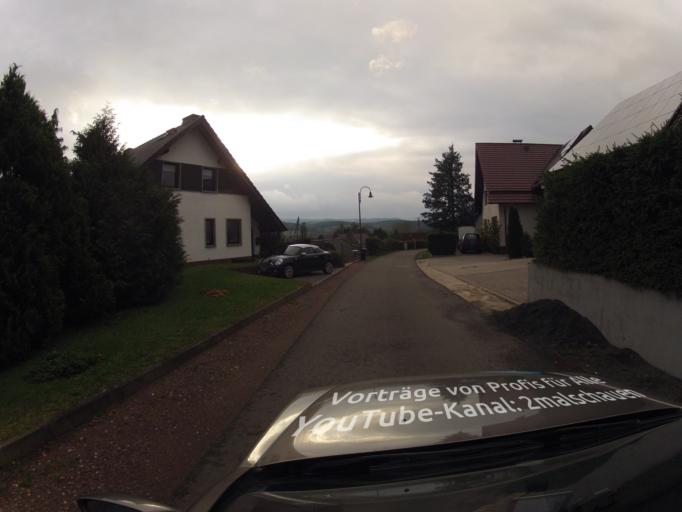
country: DE
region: Thuringia
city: Breitungen
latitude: 50.7600
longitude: 10.3362
